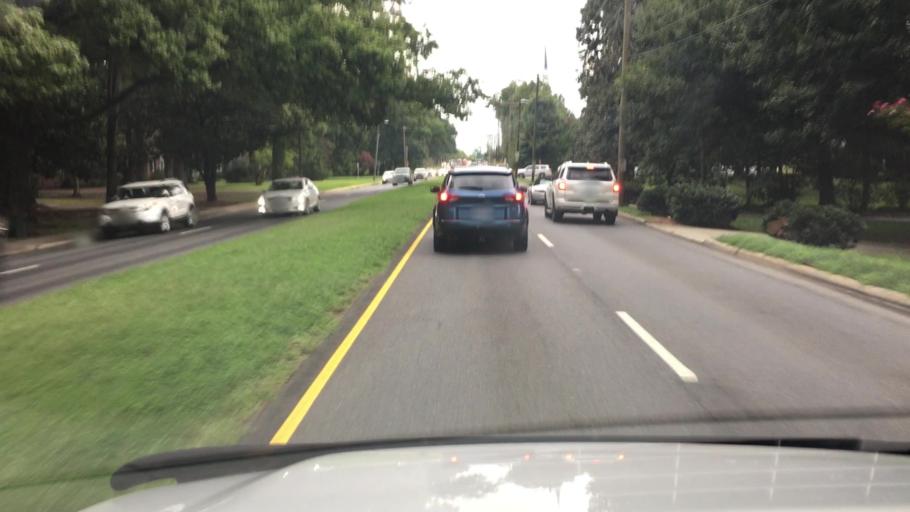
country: US
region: North Carolina
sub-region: Mecklenburg County
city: Charlotte
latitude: 35.1737
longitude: -80.8121
